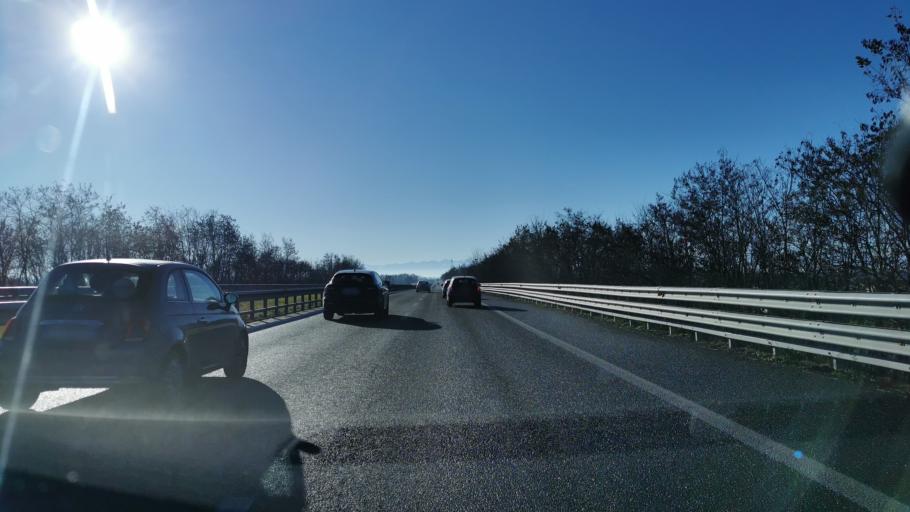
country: IT
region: Piedmont
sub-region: Provincia di Cuneo
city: Caramagna Piemonte
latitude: 44.8083
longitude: 7.7517
